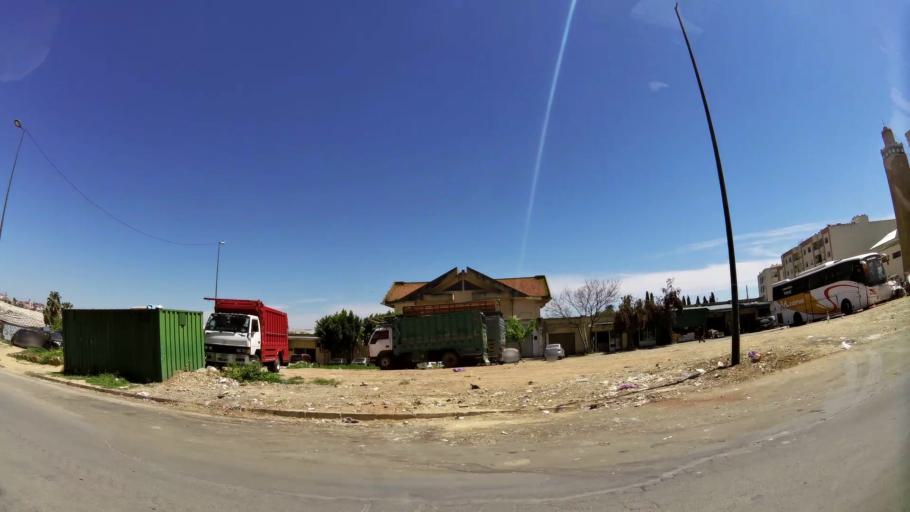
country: MA
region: Meknes-Tafilalet
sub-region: Meknes
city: Meknes
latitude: 33.8954
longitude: -5.5778
